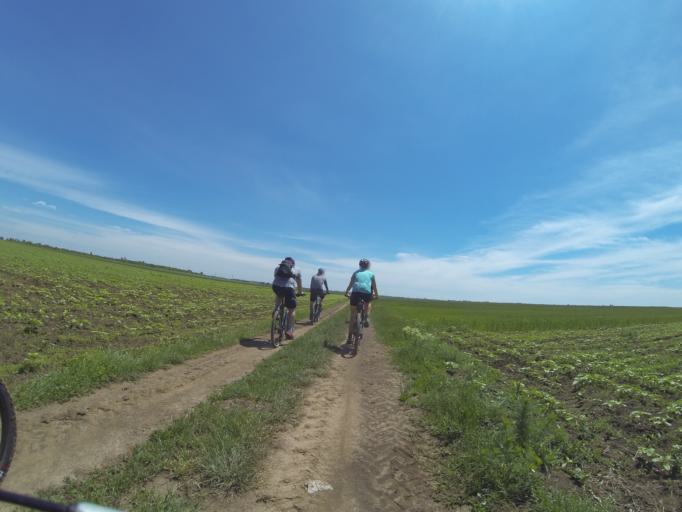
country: RO
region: Dolj
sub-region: Comuna Leu
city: Zanoaga
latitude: 44.1785
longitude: 24.0829
